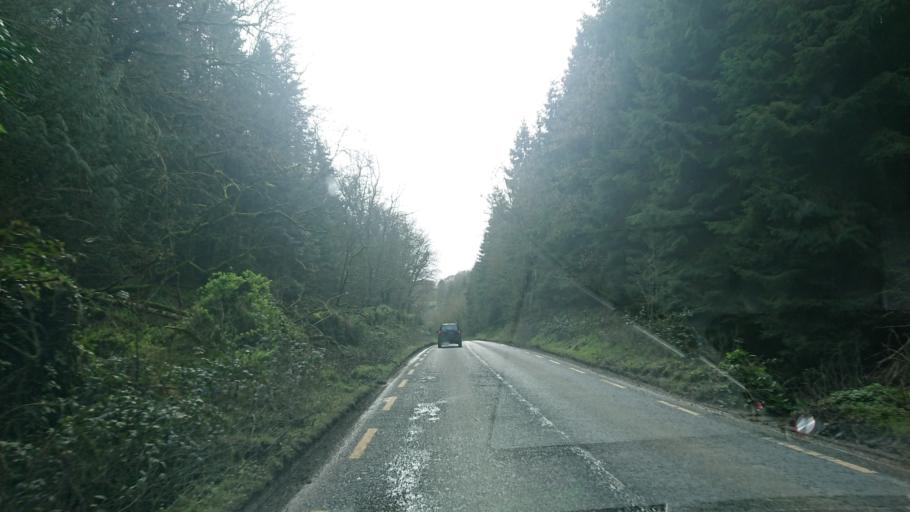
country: IE
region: Leinster
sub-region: Kildare
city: Eadestown
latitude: 53.1822
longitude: -6.5594
